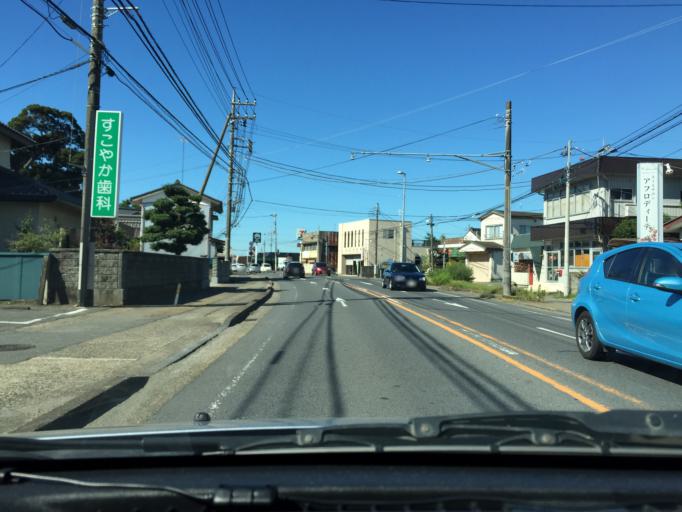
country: JP
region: Ibaraki
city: Naka
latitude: 36.0694
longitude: 140.1856
